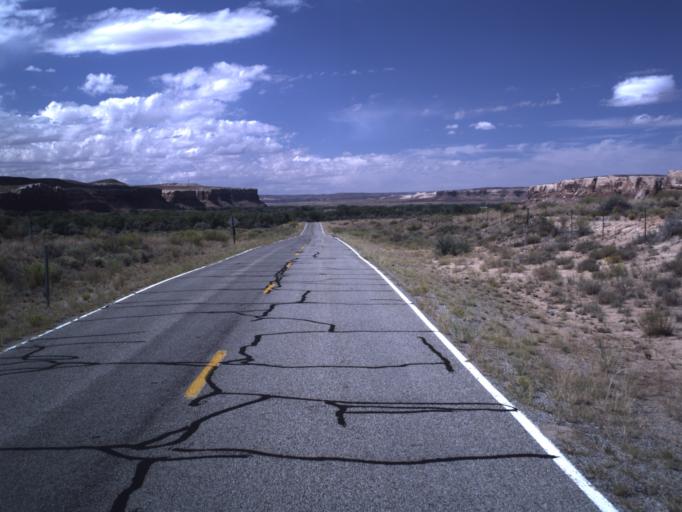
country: US
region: Utah
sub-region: San Juan County
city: Blanding
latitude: 37.2833
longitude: -109.4999
